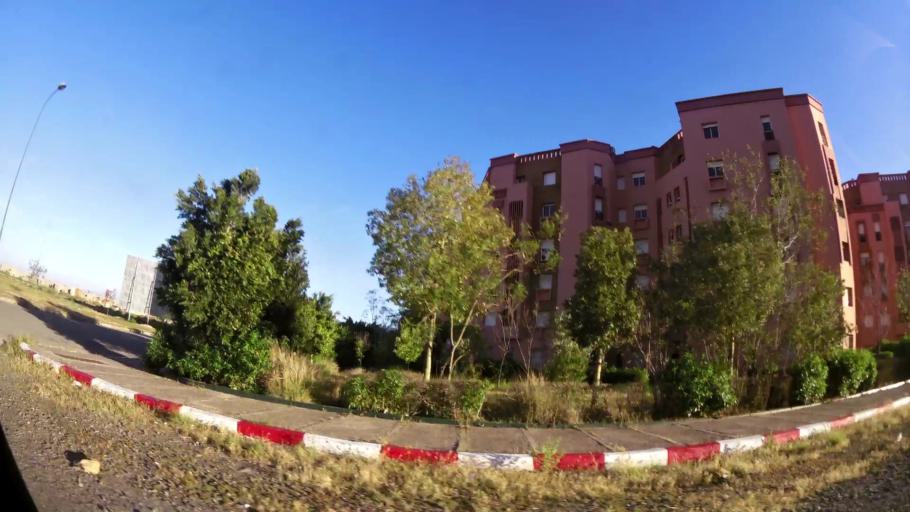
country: MA
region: Marrakech-Tensift-Al Haouz
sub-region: Marrakech
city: Marrakesh
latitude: 31.7477
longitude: -8.1287
